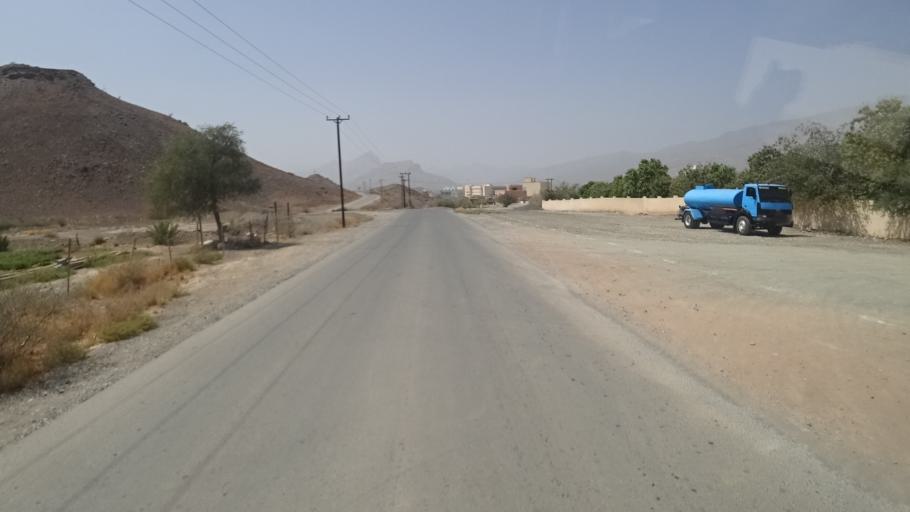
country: OM
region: Muhafazat ad Dakhiliyah
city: Bahla'
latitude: 23.0840
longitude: 57.3210
